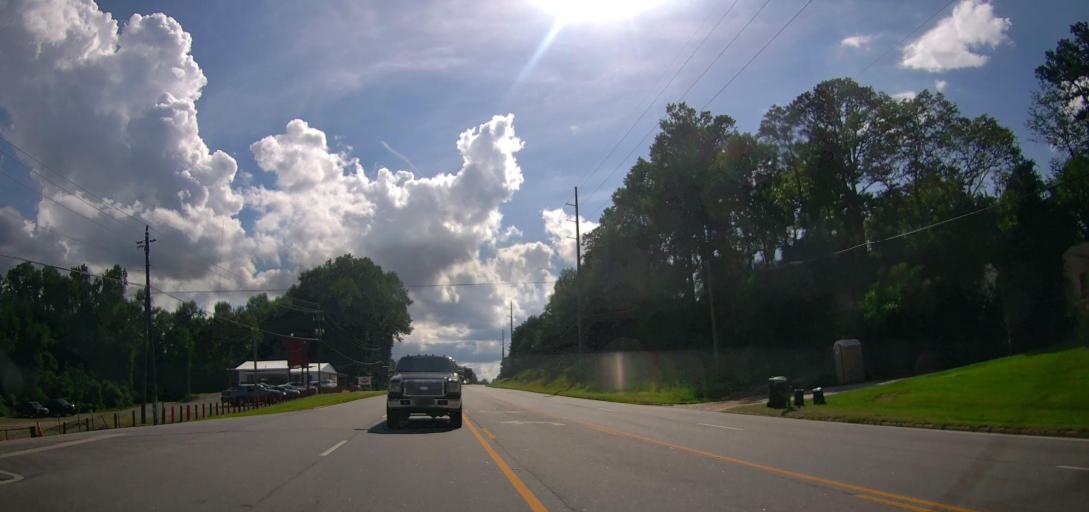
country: US
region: Alabama
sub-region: Russell County
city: Ladonia
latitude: 32.4727
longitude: -85.0476
